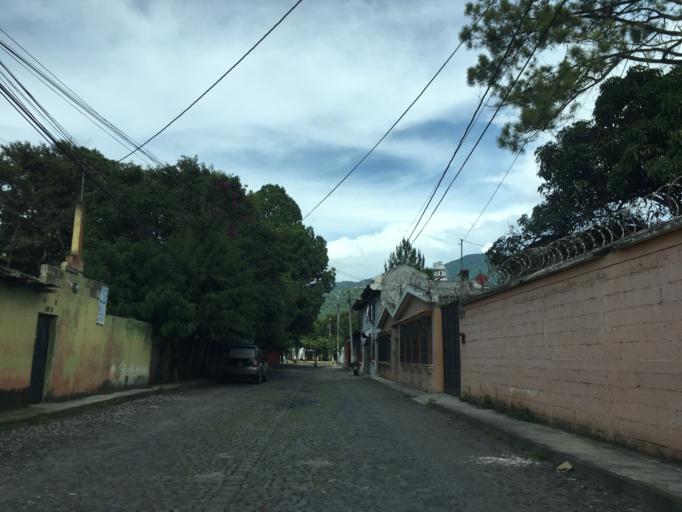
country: GT
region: Sacatepequez
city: Antigua Guatemala
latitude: 14.5422
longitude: -90.7447
